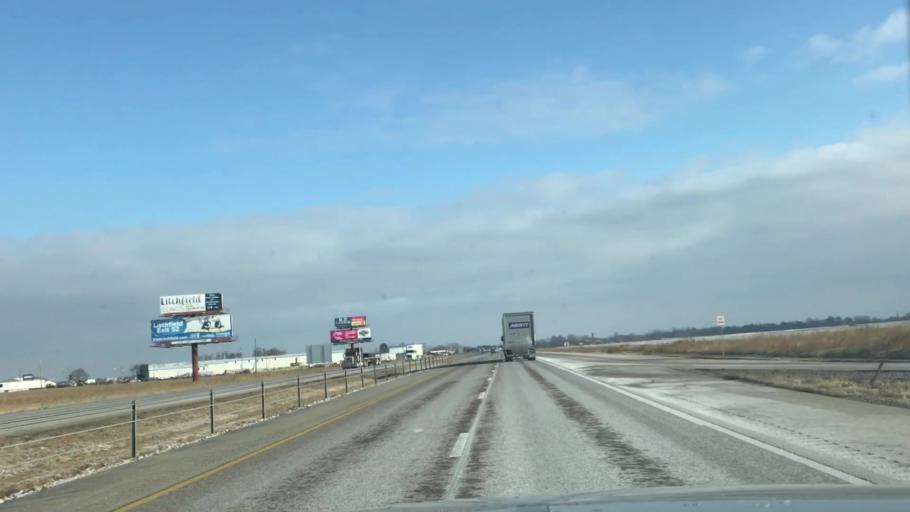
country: US
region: Illinois
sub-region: Madison County
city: Worden
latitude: 38.8914
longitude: -89.8365
